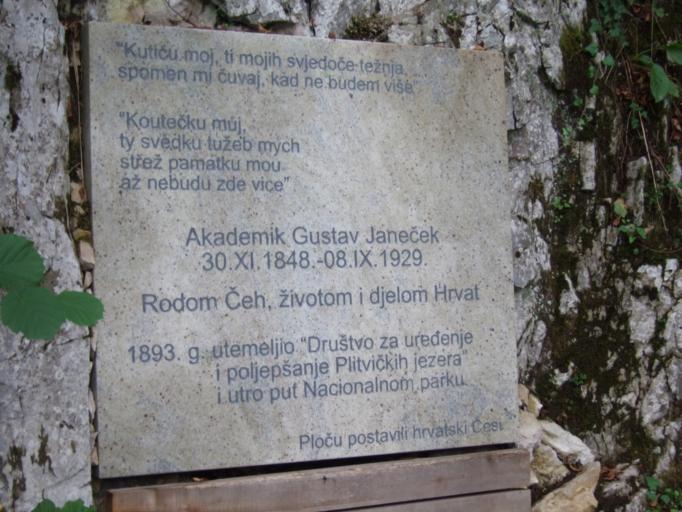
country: HR
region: Licko-Senjska
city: Jezerce
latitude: 44.8952
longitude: 15.6101
